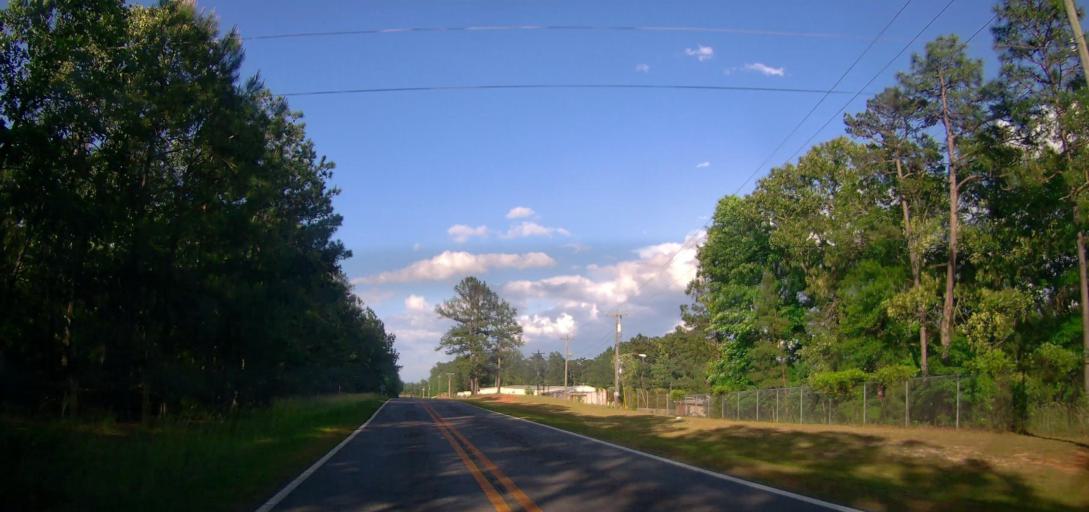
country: US
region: Georgia
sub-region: Peach County
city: Byron
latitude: 32.6714
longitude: -83.7913
